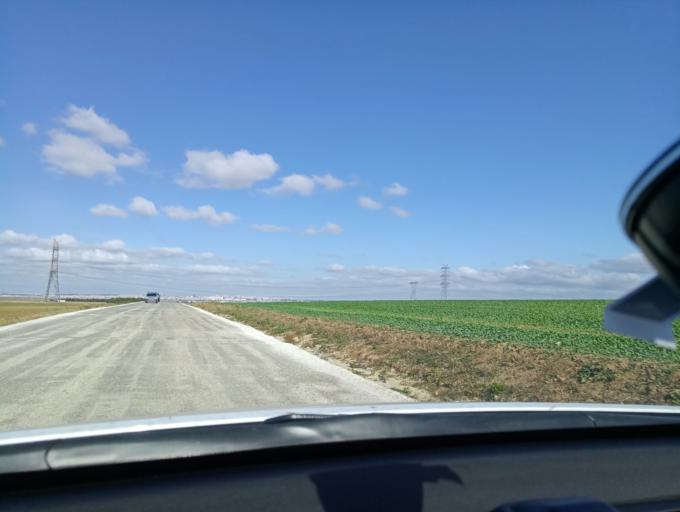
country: TR
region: Tekirdag
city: Corlu
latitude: 41.0563
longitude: 27.8349
